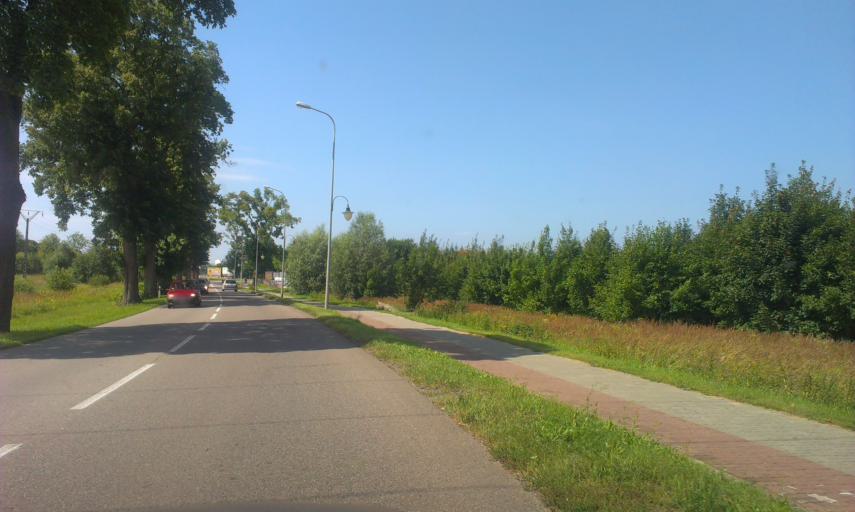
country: PL
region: West Pomeranian Voivodeship
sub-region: Powiat kolobrzeski
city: Kolobrzeg
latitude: 54.1665
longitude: 15.5967
